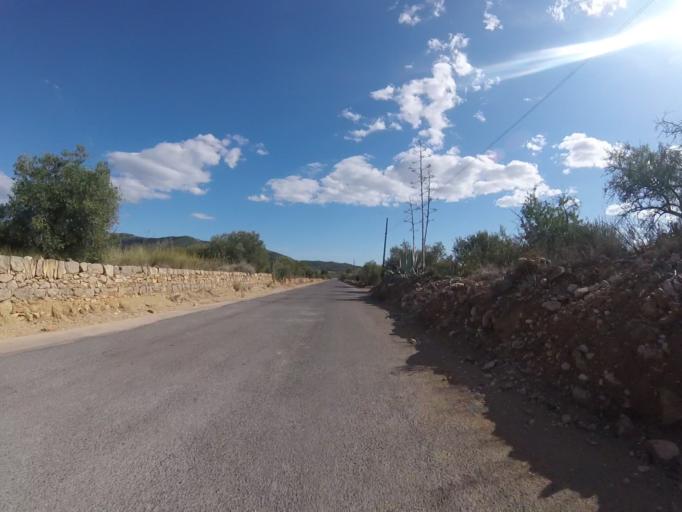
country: ES
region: Valencia
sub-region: Provincia de Castello
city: Alcala de Xivert
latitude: 40.2723
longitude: 0.2367
